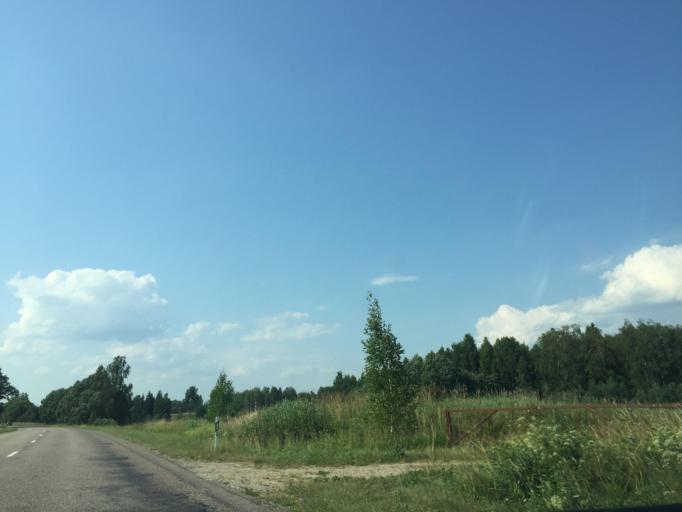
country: LV
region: Limbazu Rajons
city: Limbazi
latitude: 57.4816
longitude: 24.8707
